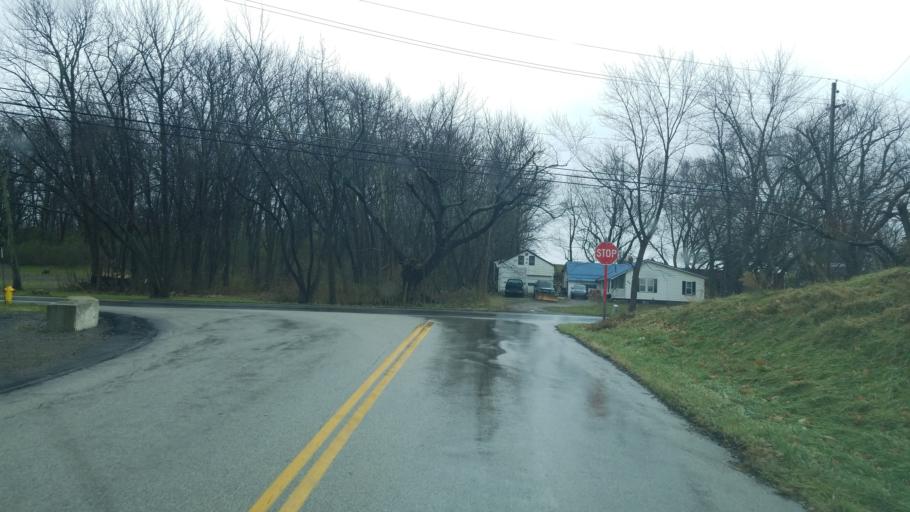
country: US
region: Ohio
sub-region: Ashtabula County
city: Edgewood
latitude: 41.8744
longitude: -80.7322
